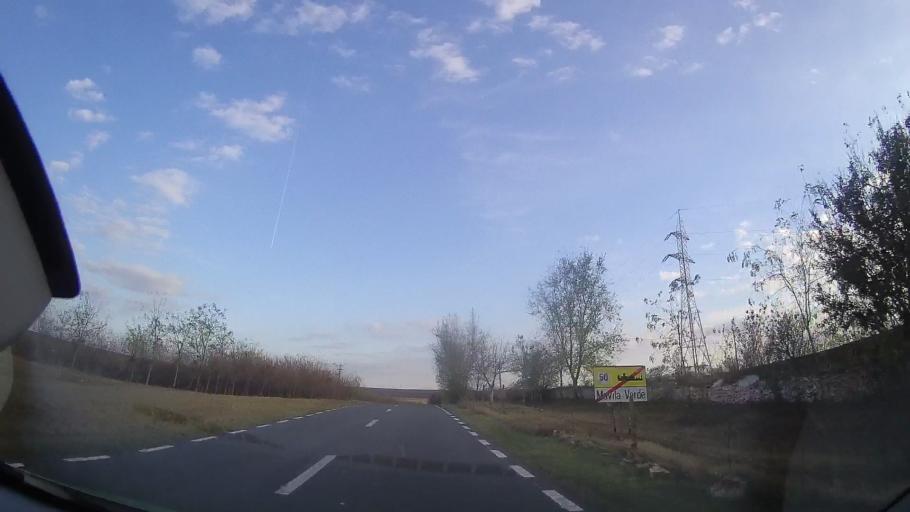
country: RO
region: Constanta
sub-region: Comuna Chirnogeni
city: Plopeni
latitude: 43.9583
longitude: 28.1466
